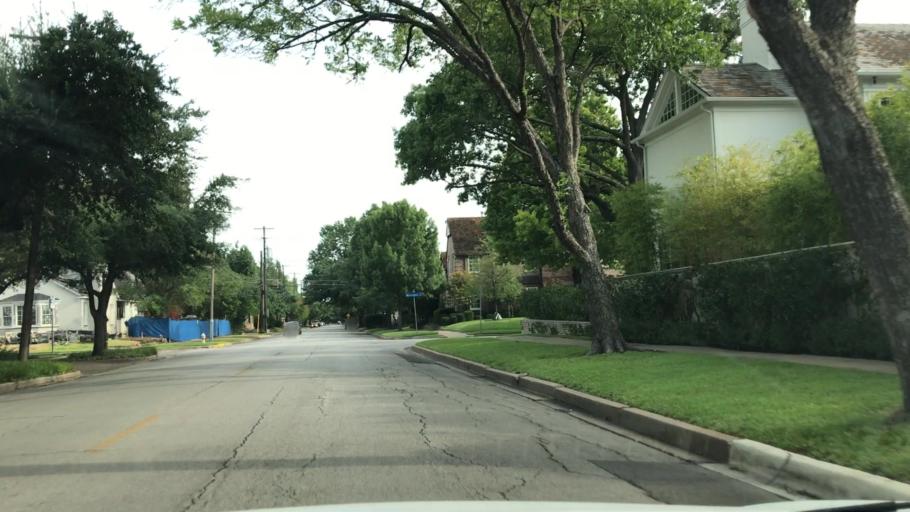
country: US
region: Texas
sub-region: Dallas County
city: Highland Park
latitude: 32.8242
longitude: -96.8070
